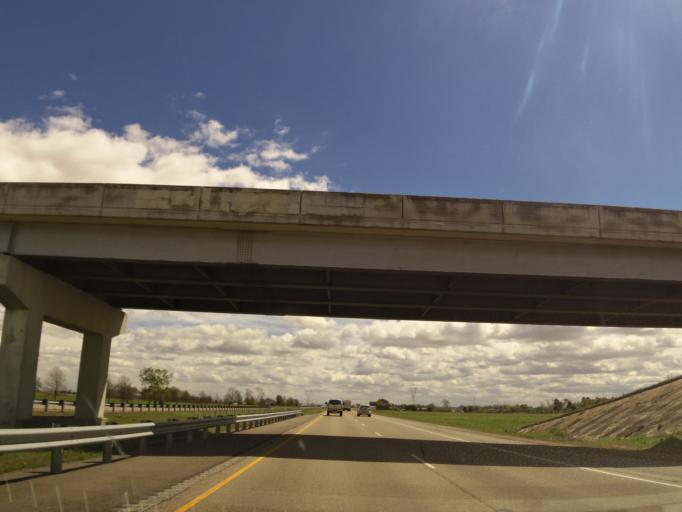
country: US
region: Arkansas
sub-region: Craighead County
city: Bay
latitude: 35.7754
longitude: -90.5861
